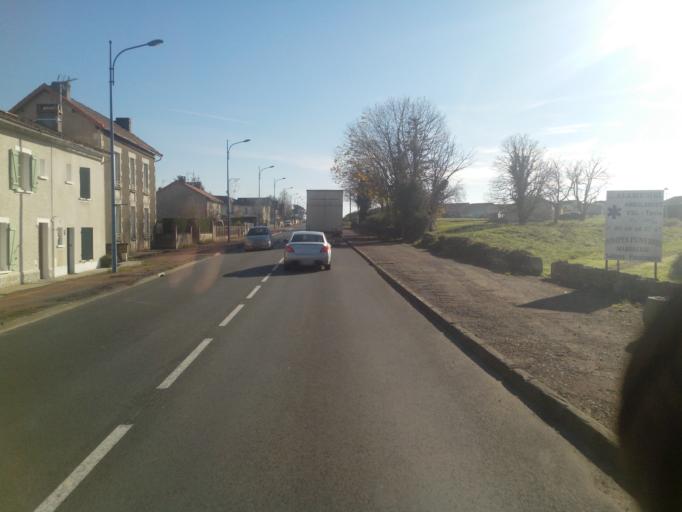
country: FR
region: Poitou-Charentes
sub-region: Departement de la Vienne
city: Lussac-les-Chateaux
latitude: 46.4007
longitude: 0.7268
